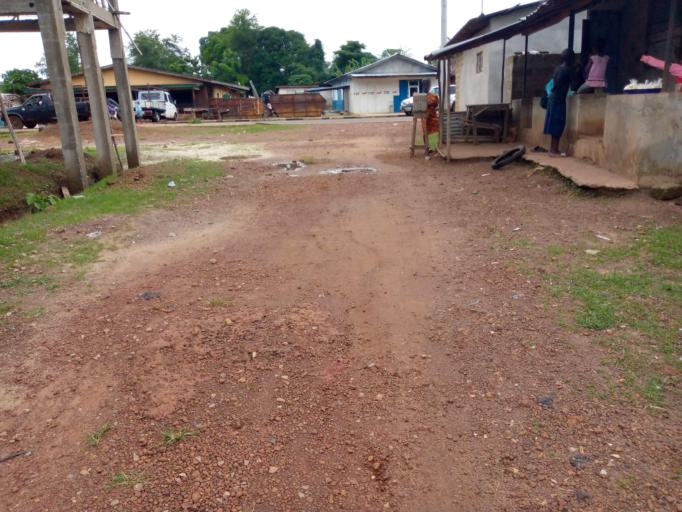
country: SL
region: Southern Province
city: Moyamba
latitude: 8.1602
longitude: -12.4351
